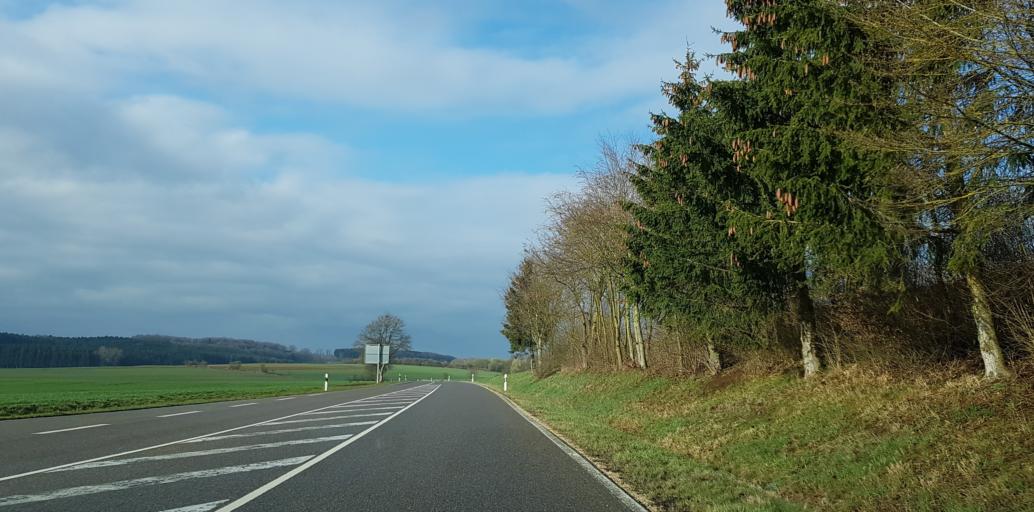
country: DE
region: Baden-Wuerttemberg
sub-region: Tuebingen Region
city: Altheim
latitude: 48.3352
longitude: 9.8065
